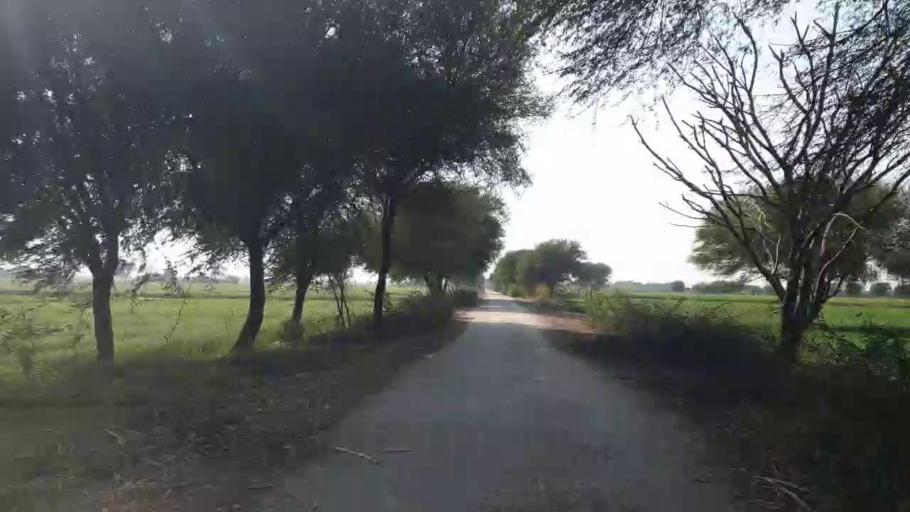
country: PK
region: Sindh
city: Mirpur Khas
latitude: 25.4130
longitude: 68.9267
